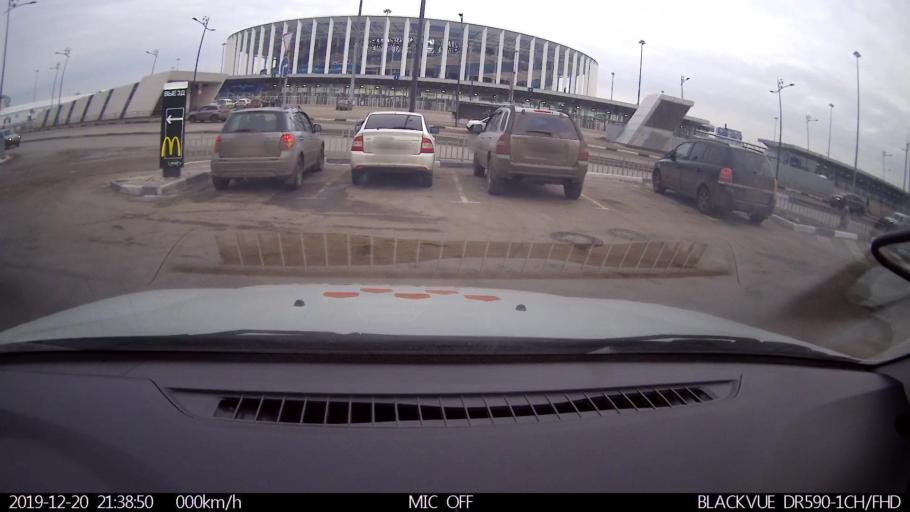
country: RU
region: Nizjnij Novgorod
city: Nizhniy Novgorod
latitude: 56.3356
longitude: 43.9666
